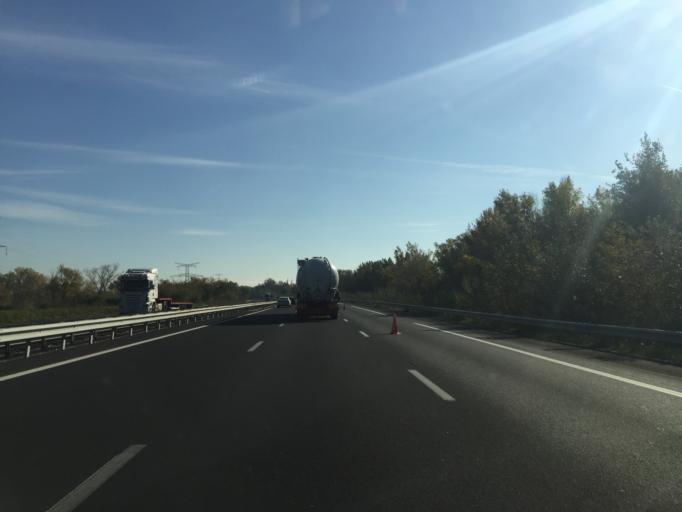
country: FR
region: Provence-Alpes-Cote d'Azur
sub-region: Departement des Bouches-du-Rhone
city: Cabannes
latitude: 43.8604
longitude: 4.9754
